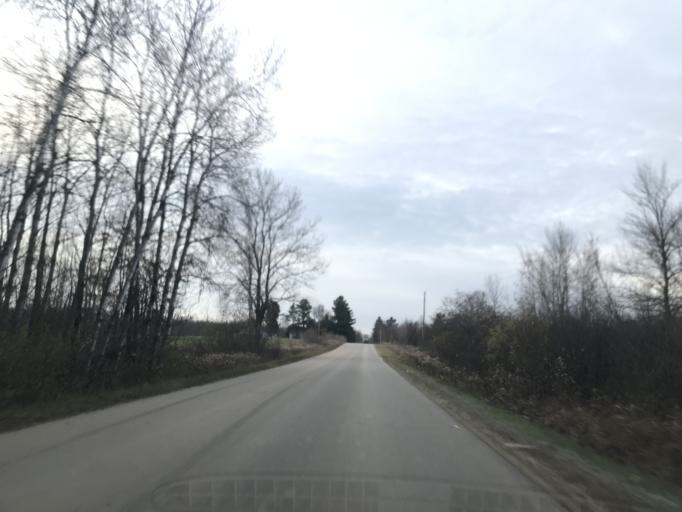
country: US
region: Wisconsin
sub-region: Marinette County
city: Peshtigo
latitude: 45.0697
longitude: -87.7995
